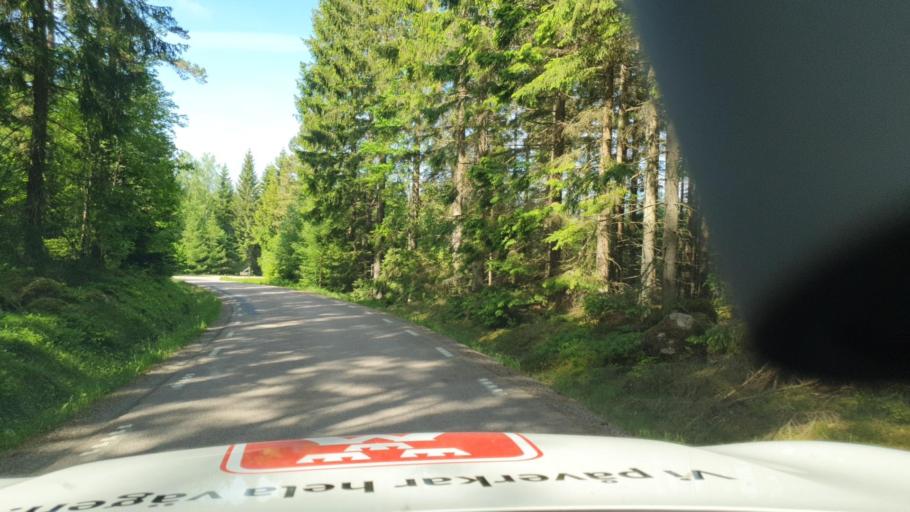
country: SE
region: Vaestra Goetaland
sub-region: Herrljunga Kommun
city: Herrljunga
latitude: 57.9259
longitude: 13.0998
